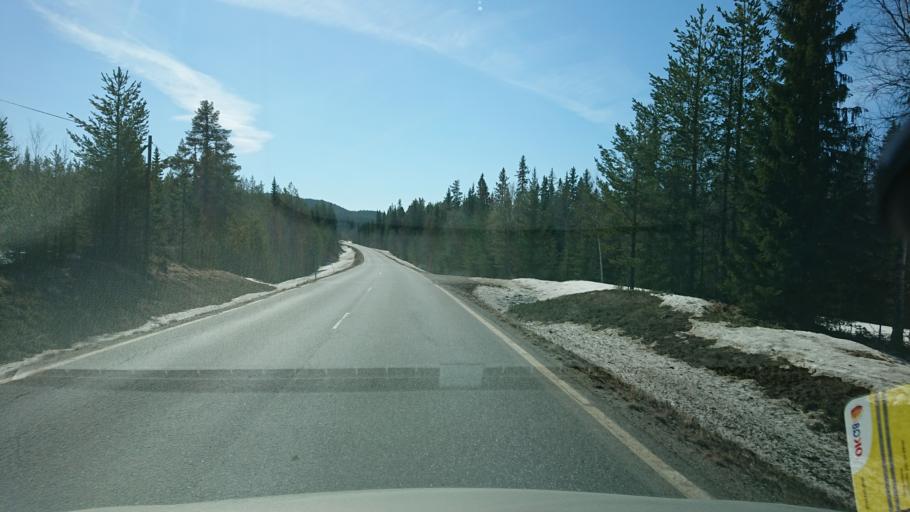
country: SE
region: Vaesterbotten
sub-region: Dorotea Kommun
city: Dorotea
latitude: 64.0674
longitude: 16.2572
